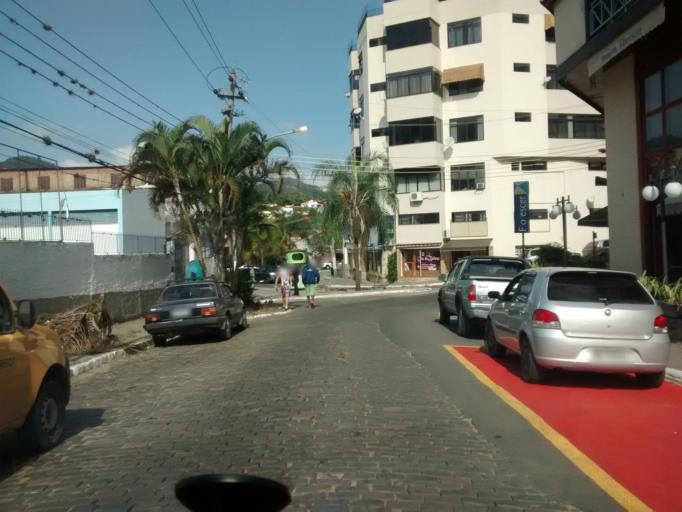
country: BR
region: Rio de Janeiro
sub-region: Miguel Pereira
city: Miguel Pereira
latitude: -22.4546
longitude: -43.4722
